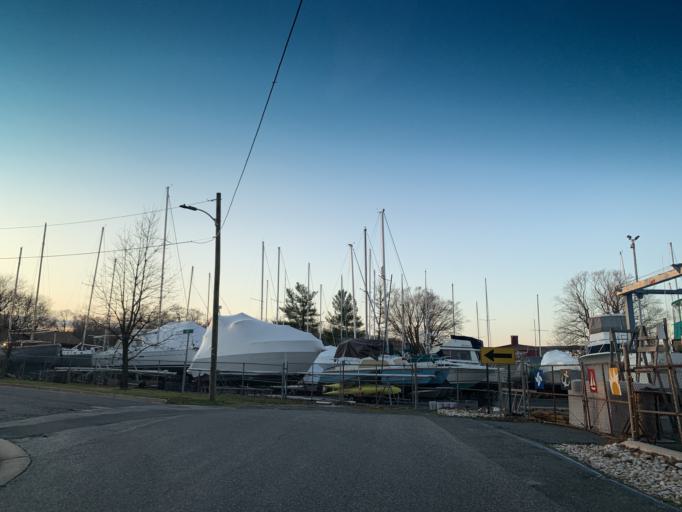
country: US
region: Maryland
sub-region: Harford County
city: Havre de Grace
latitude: 39.5552
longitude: -76.0930
